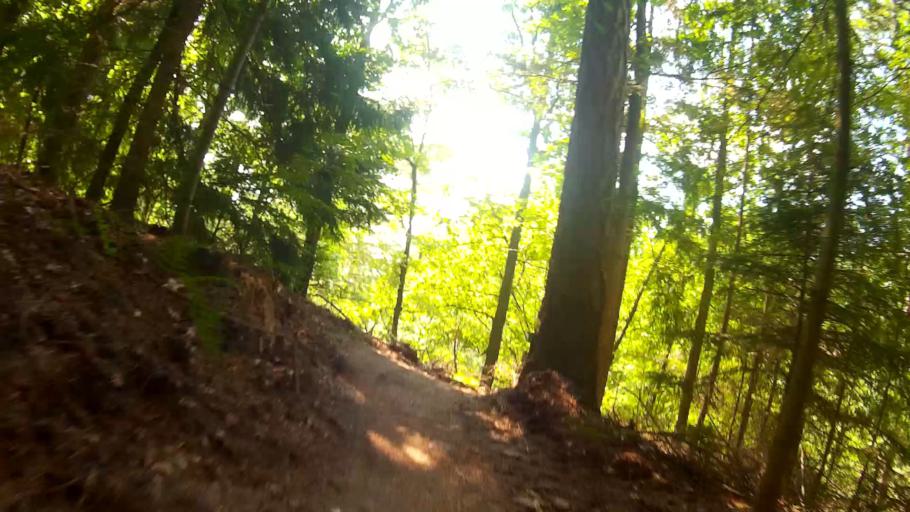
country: NL
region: North Holland
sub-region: Gemeente Laren
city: Laren
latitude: 52.2070
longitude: 5.2287
